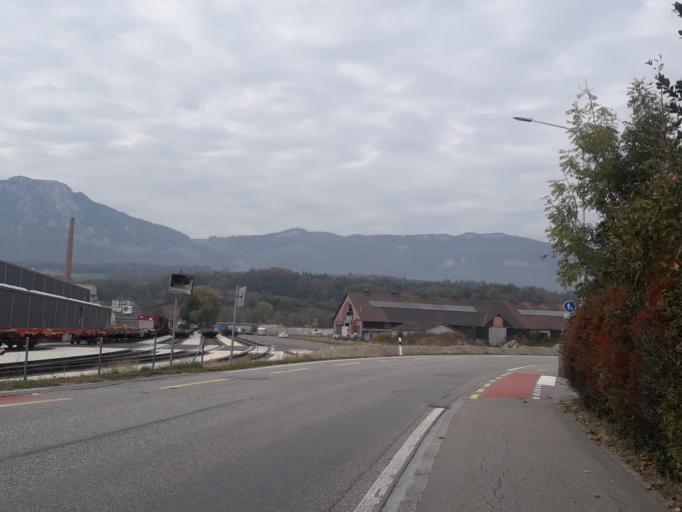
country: CH
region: Solothurn
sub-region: Bezirk Wasseramt
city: Luterbach
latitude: 47.2209
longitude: 7.5837
